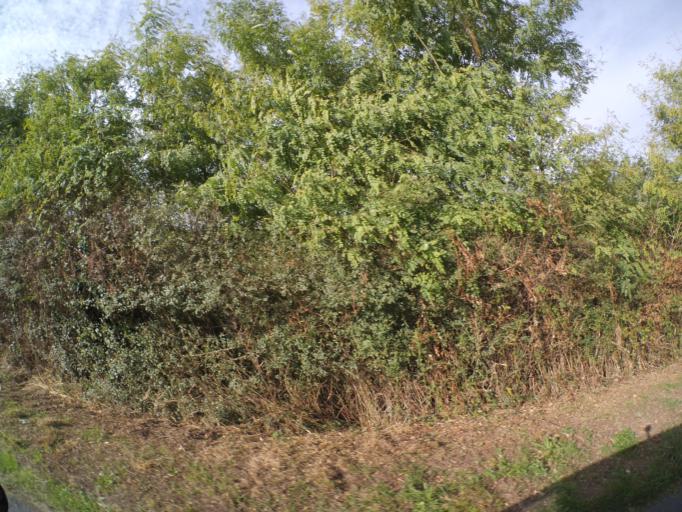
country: FR
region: Pays de la Loire
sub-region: Departement de Maine-et-Loire
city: La Chapelle-du-Genet
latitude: 47.1876
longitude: -1.0311
